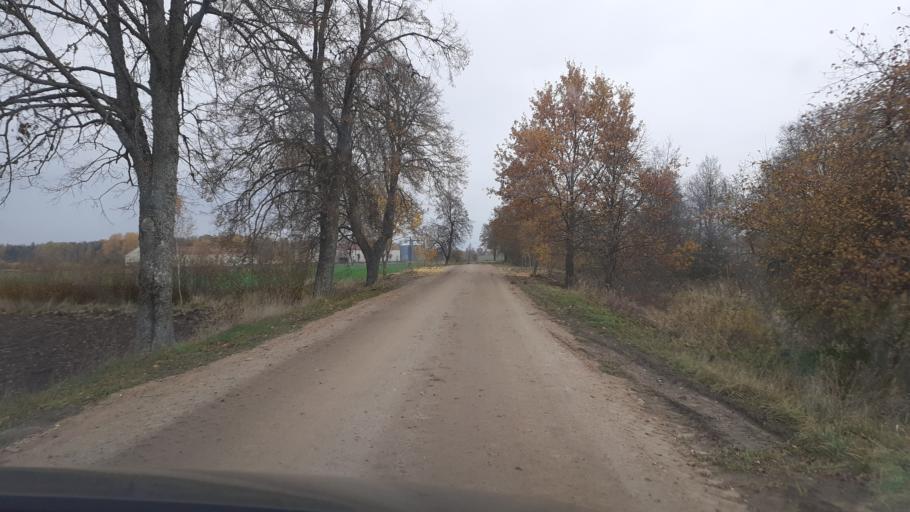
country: LV
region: Skrunda
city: Skrunda
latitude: 56.8508
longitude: 22.2140
